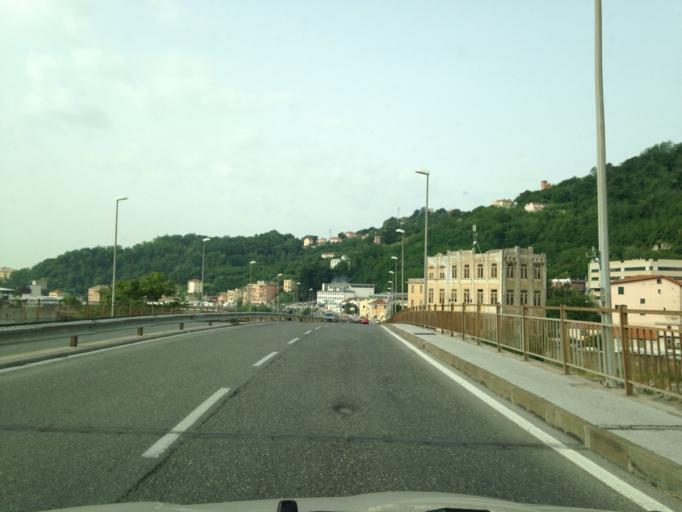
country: IT
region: Liguria
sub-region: Provincia di Genova
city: Manesseno
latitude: 44.4670
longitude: 8.9001
